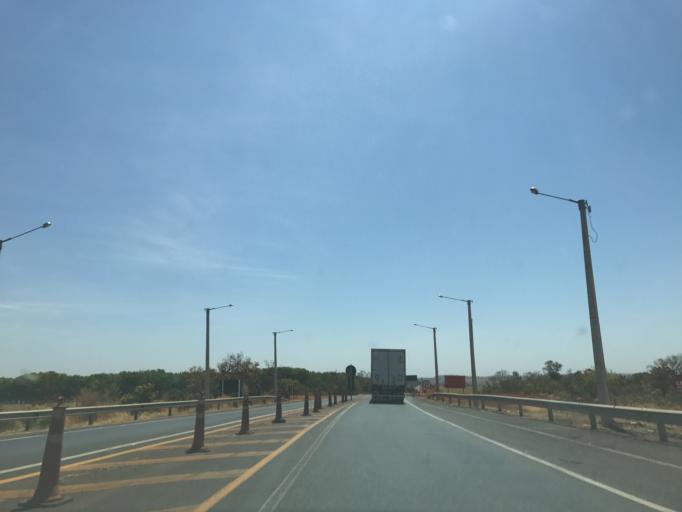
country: BR
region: Minas Gerais
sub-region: Prata
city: Prata
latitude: -19.4699
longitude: -48.8722
